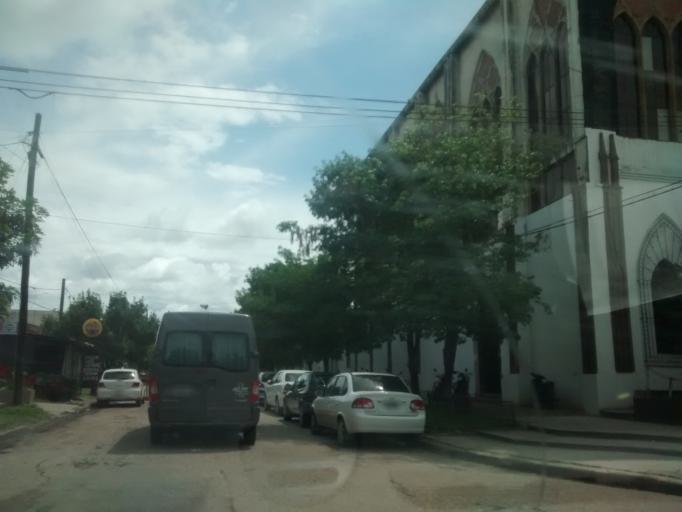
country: AR
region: Chaco
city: Resistencia
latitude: -27.4463
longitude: -58.9988
